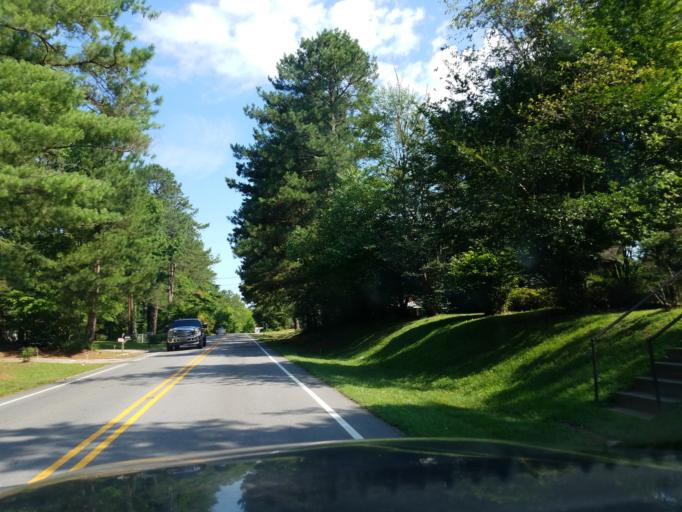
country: US
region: North Carolina
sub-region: Vance County
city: Henderson
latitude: 36.3444
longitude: -78.4128
